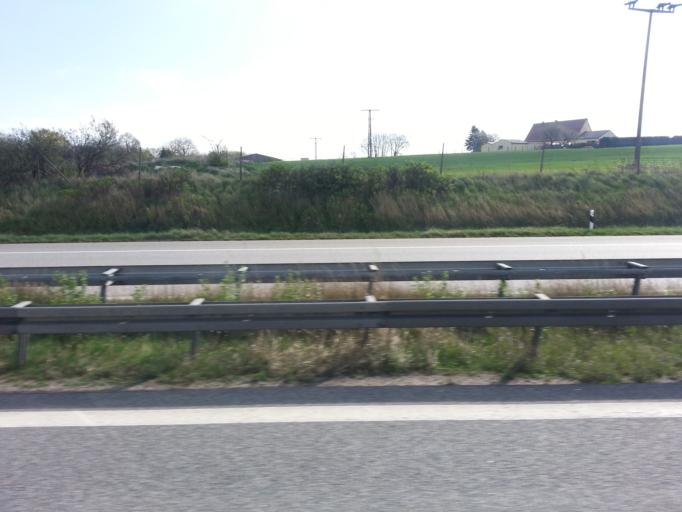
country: DE
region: Mecklenburg-Vorpommern
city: Lalendorf
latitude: 53.7167
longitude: 12.3568
